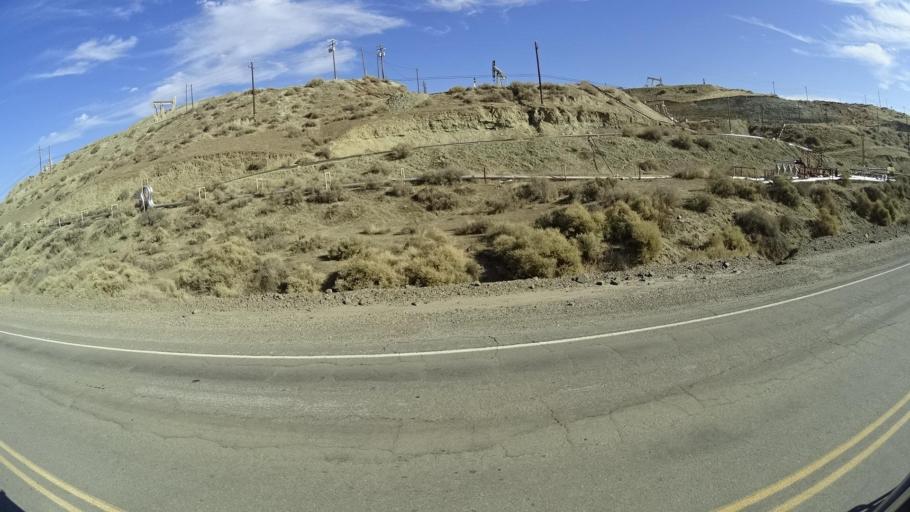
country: US
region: California
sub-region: Kern County
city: Oildale
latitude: 35.5839
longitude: -118.9596
